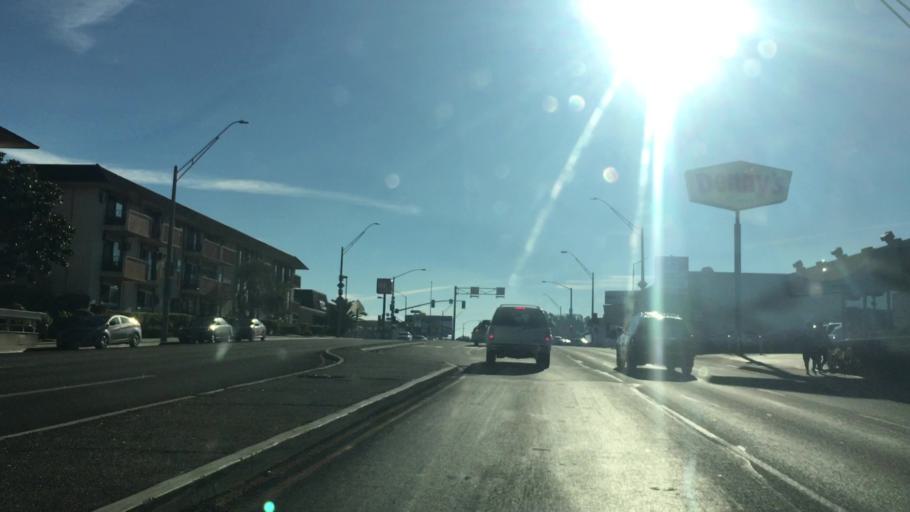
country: US
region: California
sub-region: Orange County
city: Seal Beach
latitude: 33.7762
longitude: -118.1240
